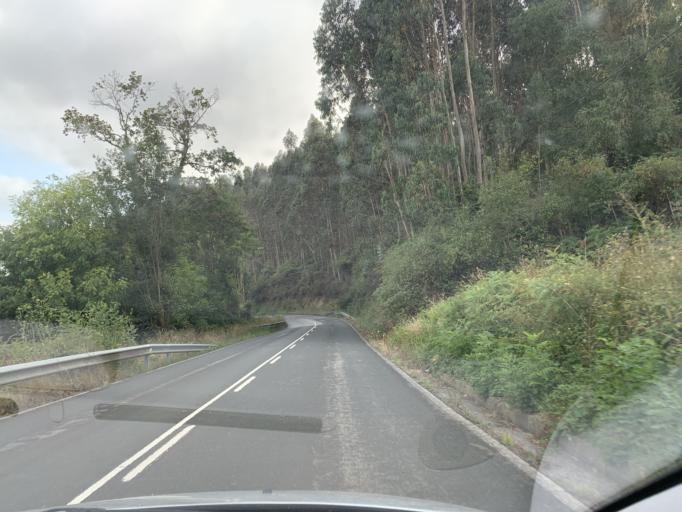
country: ES
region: Asturias
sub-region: Province of Asturias
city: Villaviciosa
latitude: 43.5118
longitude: -5.4267
